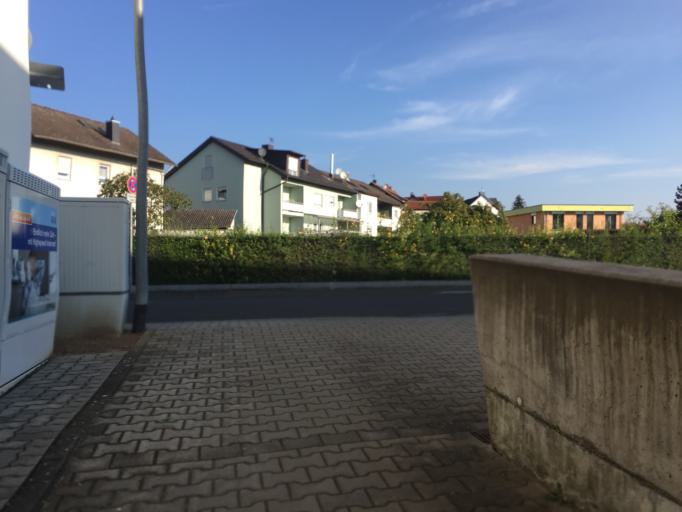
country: DE
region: Bavaria
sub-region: Regierungsbezirk Unterfranken
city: Goldbach
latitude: 49.9955
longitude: 9.1824
